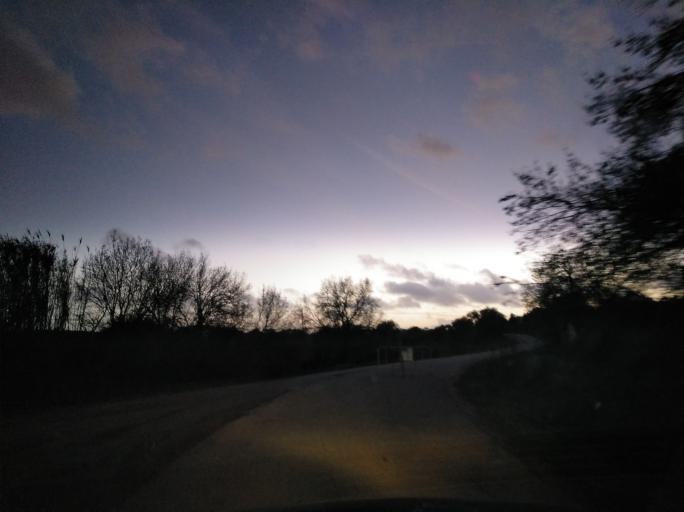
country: PT
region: Portalegre
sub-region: Campo Maior
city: Campo Maior
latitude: 39.0797
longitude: -7.0189
